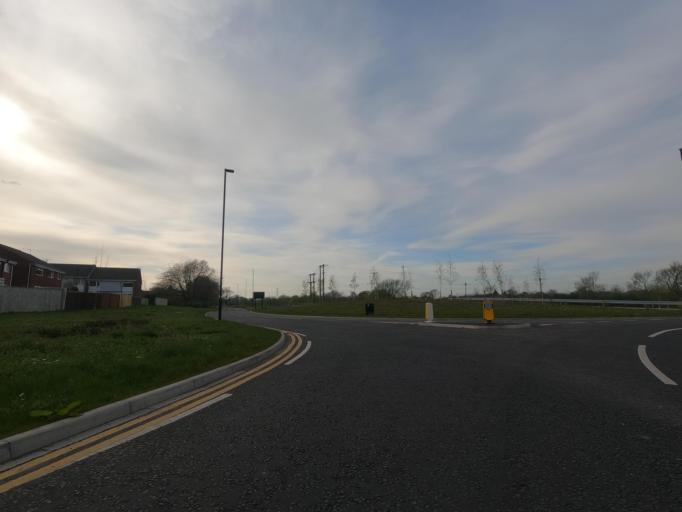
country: GB
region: England
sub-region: Newcastle upon Tyne
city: Hazlerigg
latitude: 55.0217
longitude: -1.6624
